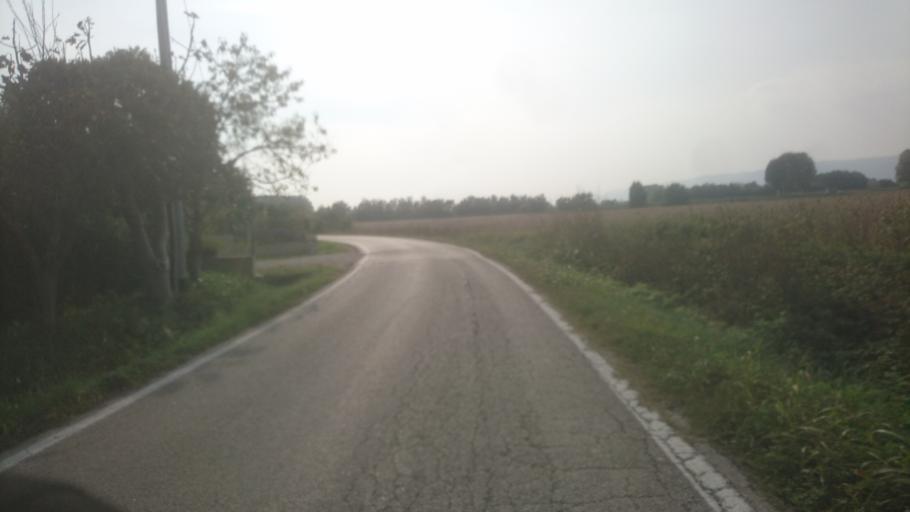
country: IT
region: Veneto
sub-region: Provincia di Vicenza
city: Montegalda
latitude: 45.4574
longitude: 11.6557
